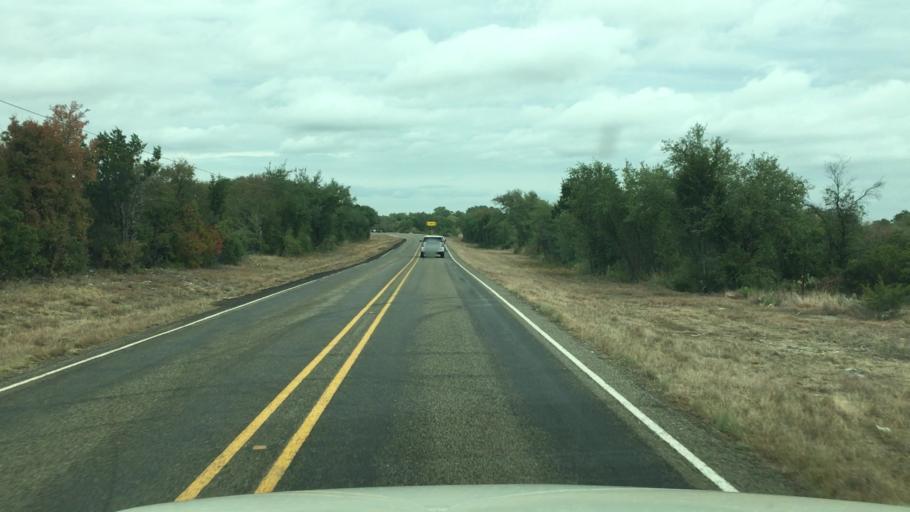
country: US
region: Texas
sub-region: Llano County
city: Horseshoe Bay
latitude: 30.4755
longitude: -98.4166
